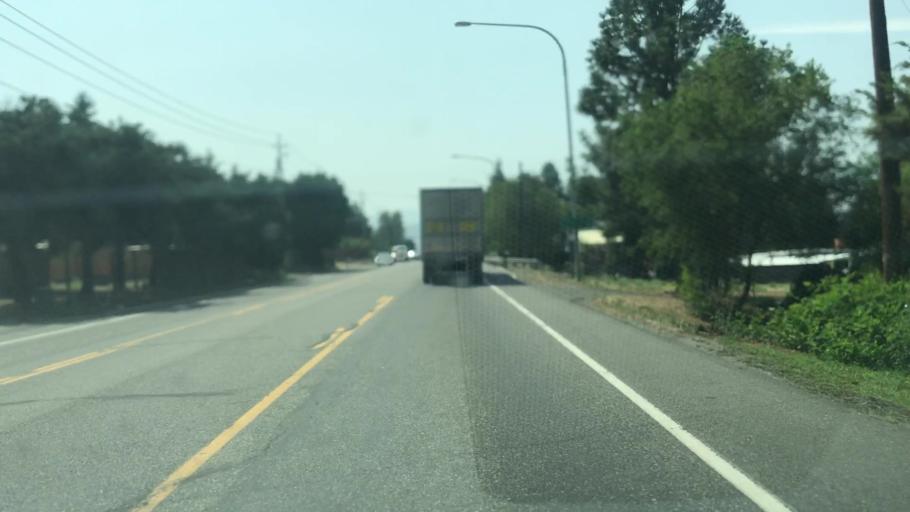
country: US
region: Washington
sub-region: Douglas County
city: East Wenatchee Bench
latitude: 47.4480
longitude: -120.2974
